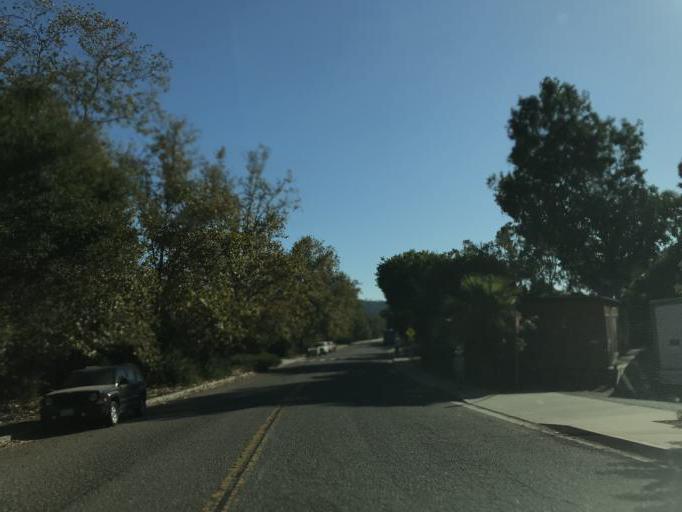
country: US
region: California
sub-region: Santa Barbara County
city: Goleta
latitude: 34.4455
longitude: -119.7794
